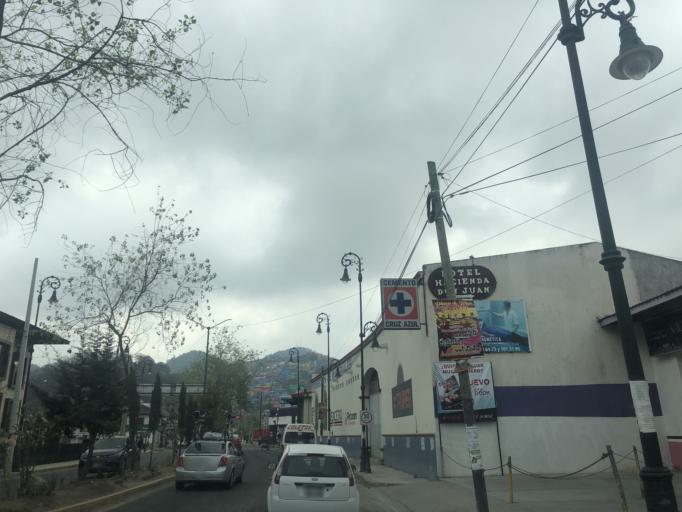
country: MX
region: Chiapas
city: San Cristobal de las Casas
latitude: 16.7209
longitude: -92.6379
